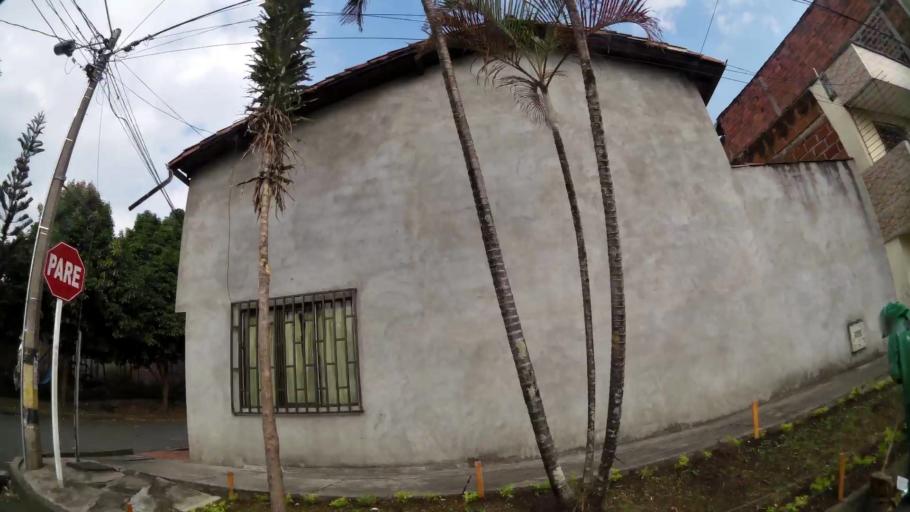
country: CO
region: Antioquia
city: Sabaneta
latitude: 6.1657
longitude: -75.6229
